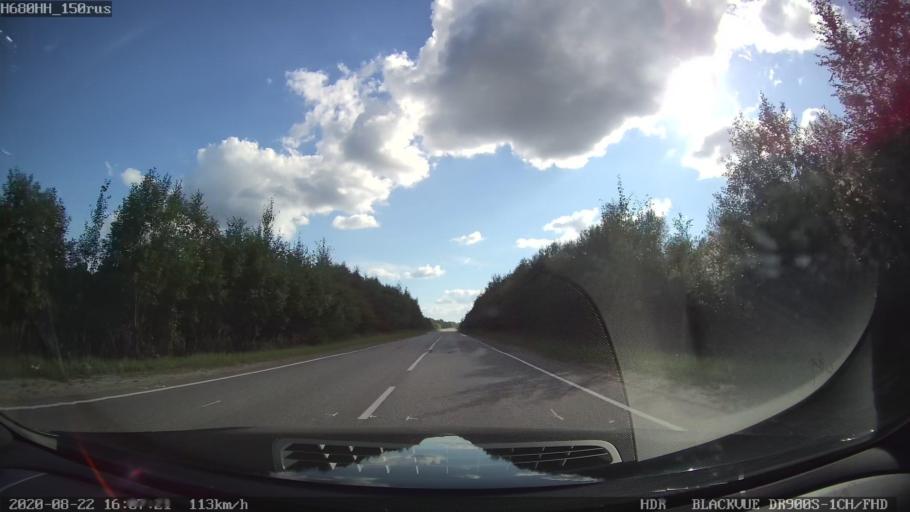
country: RU
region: Tverskaya
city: Rameshki
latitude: 57.5543
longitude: 36.3147
